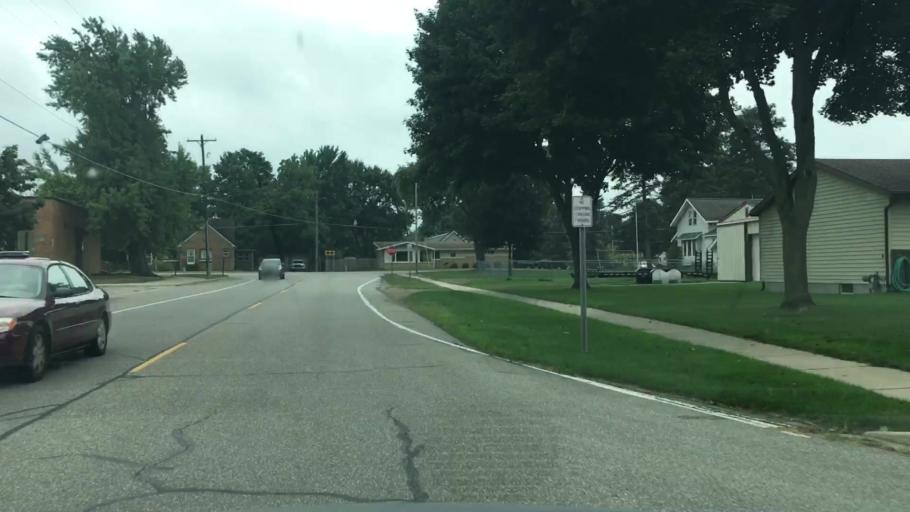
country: US
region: Michigan
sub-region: Ottawa County
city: Jenison
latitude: 42.8895
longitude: -85.8119
